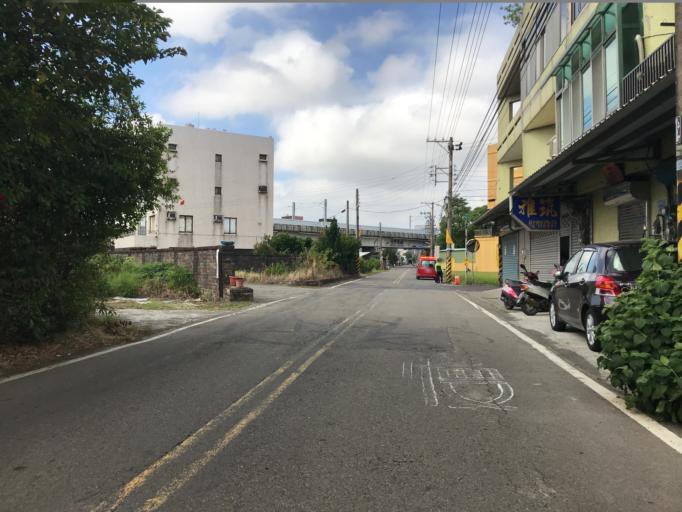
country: TW
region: Taiwan
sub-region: Hsinchu
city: Zhubei
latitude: 24.8077
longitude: 121.0034
